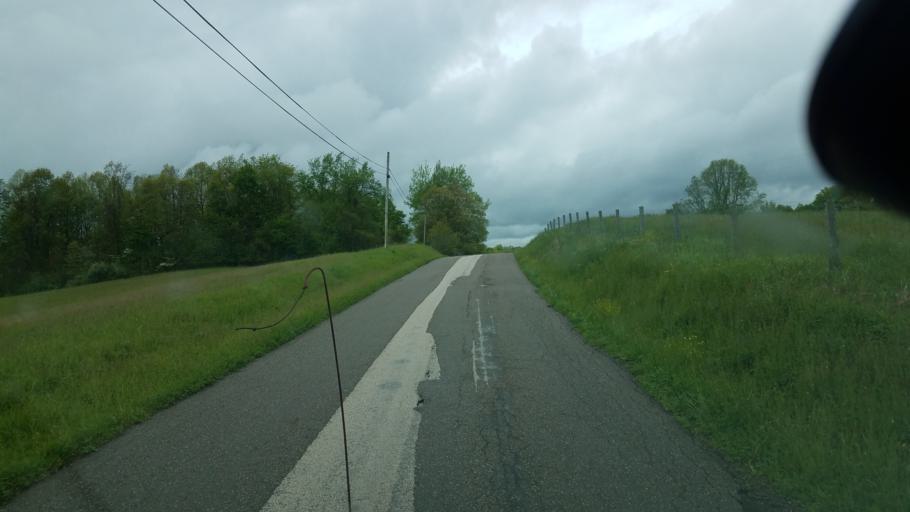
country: US
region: Ohio
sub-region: Tuscarawas County
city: Rockford
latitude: 40.4044
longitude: -81.1982
